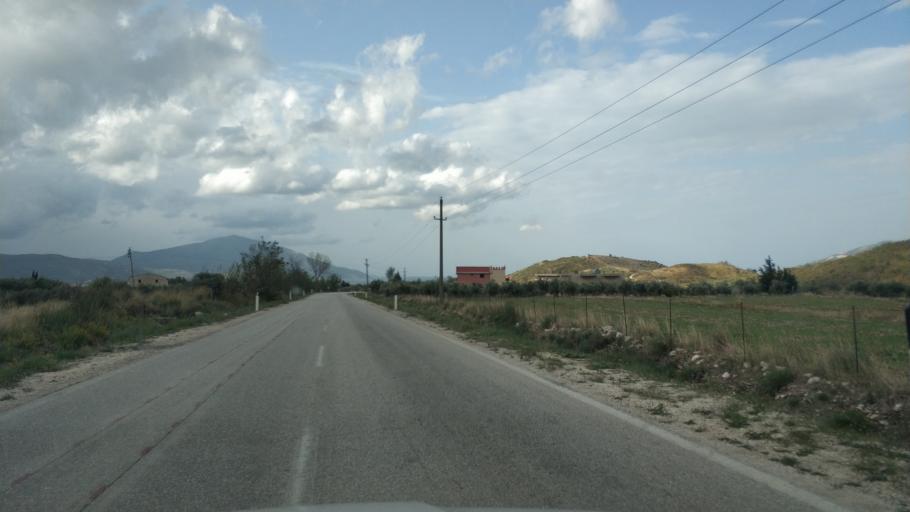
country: AL
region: Vlore
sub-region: Rrethi i Vlores
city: Orikum
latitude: 40.2874
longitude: 19.4948
